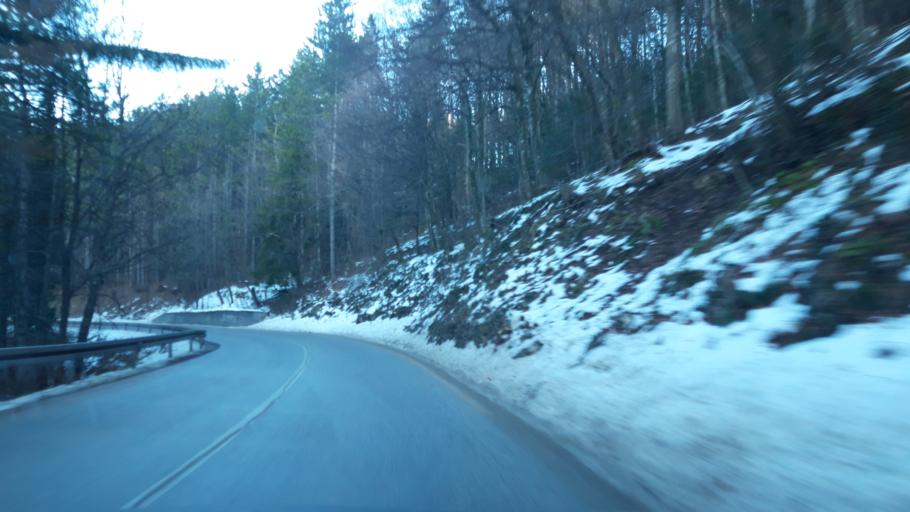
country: BA
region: Republika Srpska
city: Vlasenica
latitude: 44.1738
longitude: 18.9481
